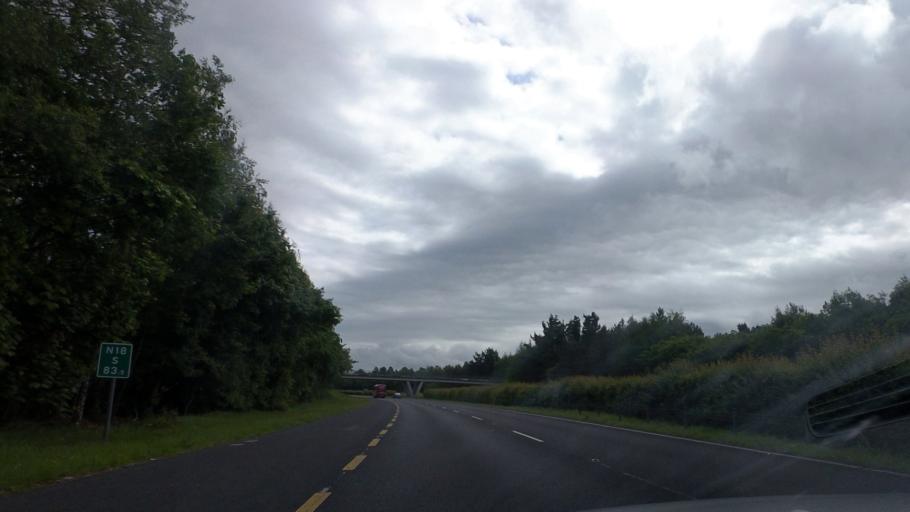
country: IE
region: Munster
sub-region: An Clar
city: Shannon
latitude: 52.6959
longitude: -8.8249
